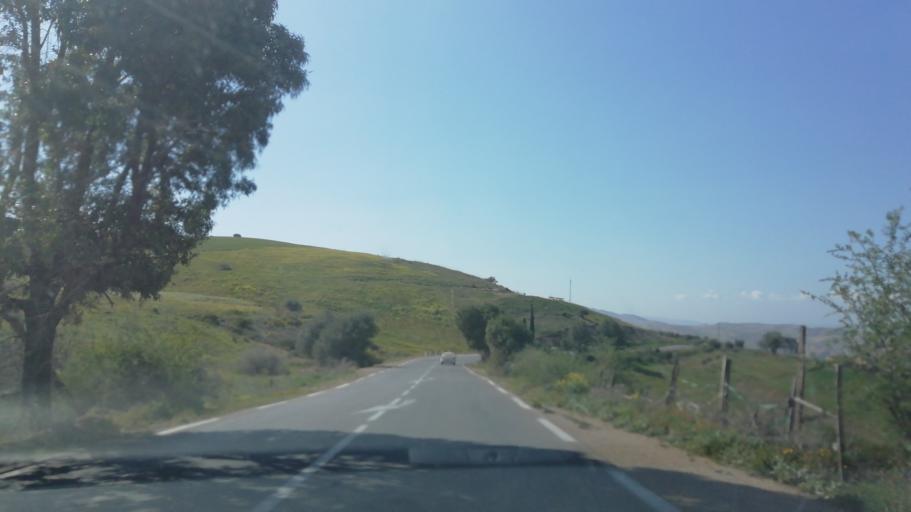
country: DZ
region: Mascara
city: Mascara
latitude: 35.5447
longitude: 0.0886
